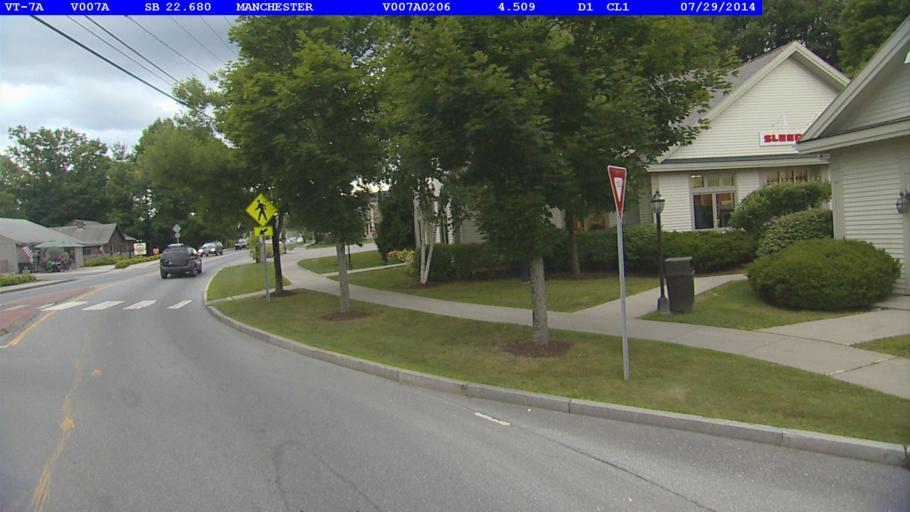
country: US
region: Vermont
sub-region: Bennington County
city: Manchester Center
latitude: 43.1731
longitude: -73.0620
